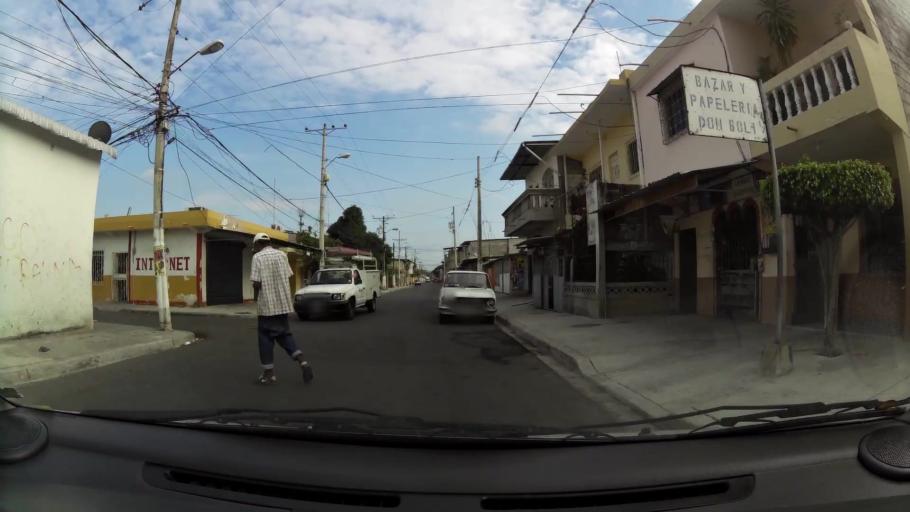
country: EC
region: Guayas
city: Guayaquil
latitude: -2.2483
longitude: -79.8816
